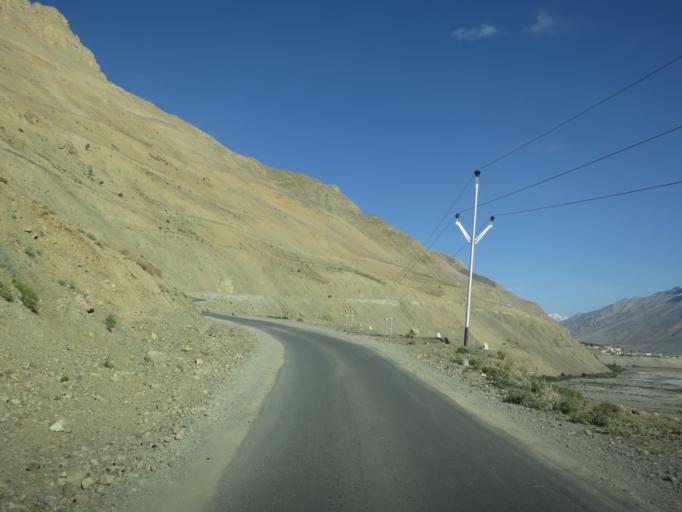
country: IN
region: Himachal Pradesh
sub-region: Shimla
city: Sarahan
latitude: 32.2439
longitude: 78.0549
